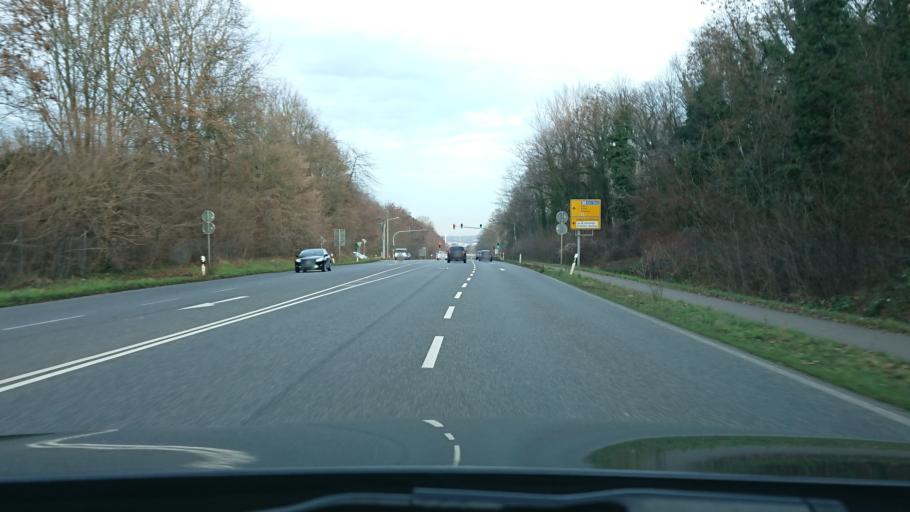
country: DE
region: North Rhine-Westphalia
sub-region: Regierungsbezirk Koln
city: Frechen
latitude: 50.8954
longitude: 6.8062
